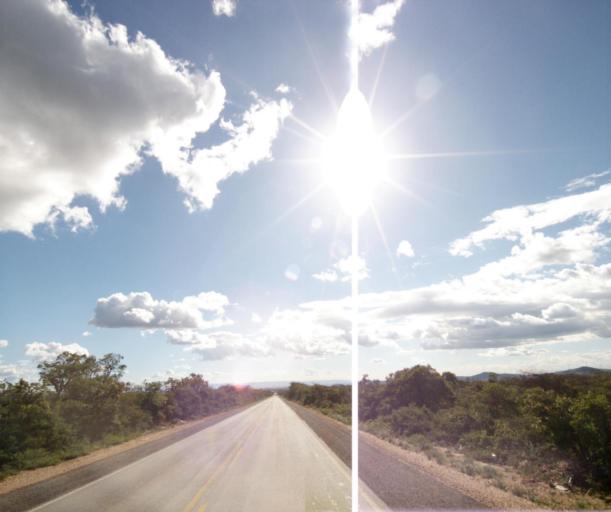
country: BR
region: Bahia
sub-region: Caetite
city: Caetite
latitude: -14.1237
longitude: -42.6151
